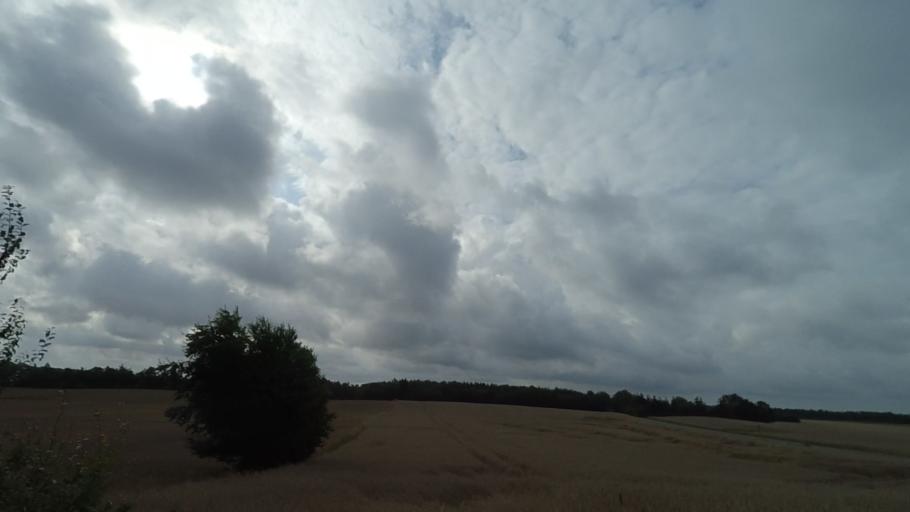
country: DK
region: Central Jutland
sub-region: Syddjurs Kommune
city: Ryomgard
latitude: 56.4003
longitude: 10.5024
